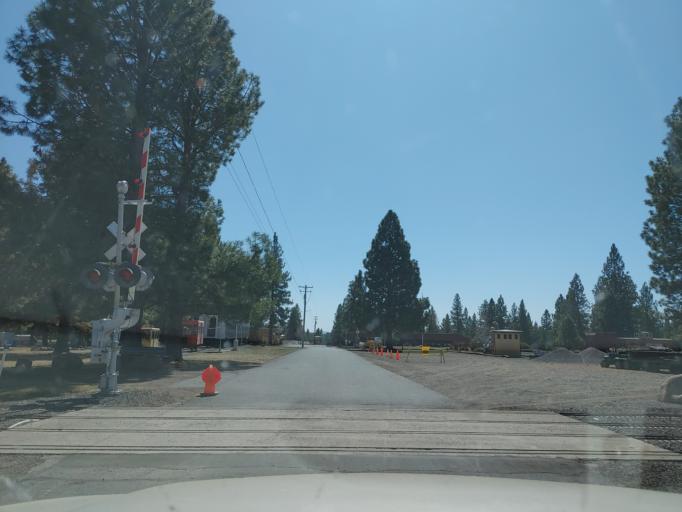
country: US
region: Oregon
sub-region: Klamath County
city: Klamath Falls
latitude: 42.5588
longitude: -121.8869
